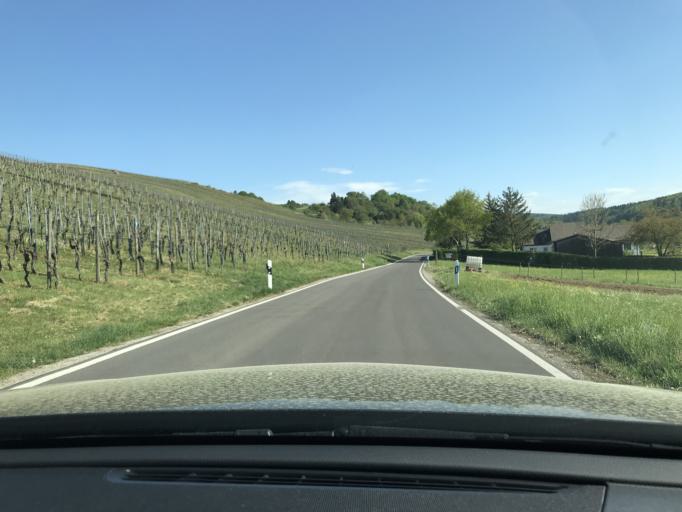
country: DE
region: Baden-Wuerttemberg
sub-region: Regierungsbezirk Stuttgart
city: Weinstadt-Endersbach
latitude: 48.7835
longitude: 9.4112
